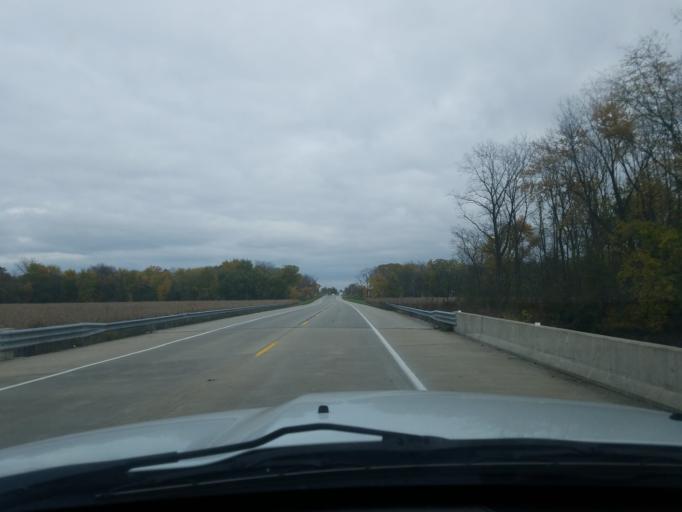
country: US
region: Indiana
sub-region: Johnson County
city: Franklin
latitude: 39.4952
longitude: -85.9545
